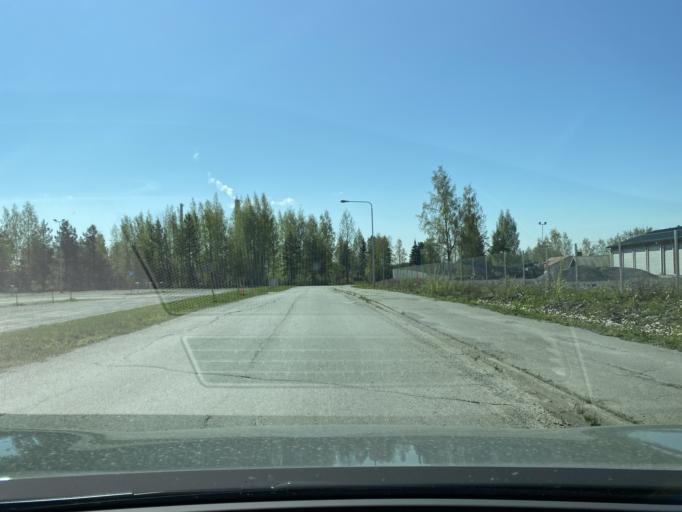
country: FI
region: Pirkanmaa
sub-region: Lounais-Pirkanmaa
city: Vammala
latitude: 61.3516
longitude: 22.8811
